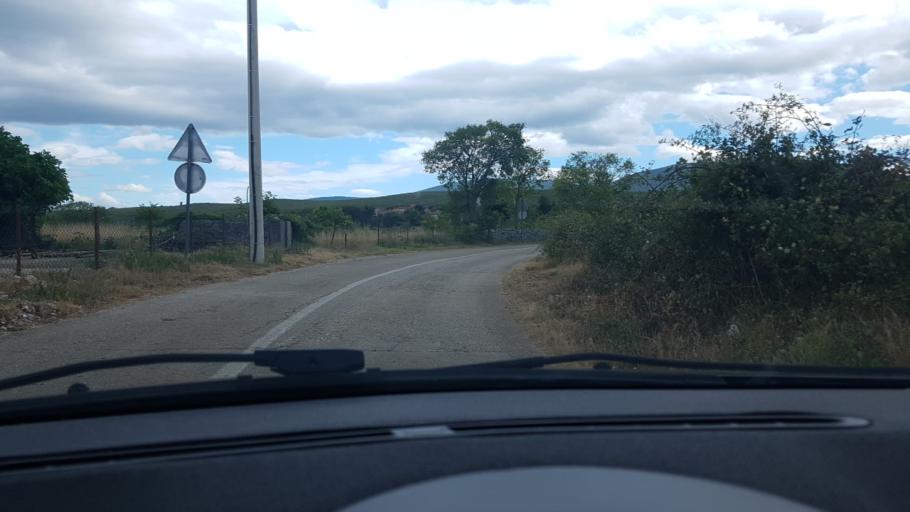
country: HR
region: Zadarska
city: Gracac
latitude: 44.1613
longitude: 15.8582
